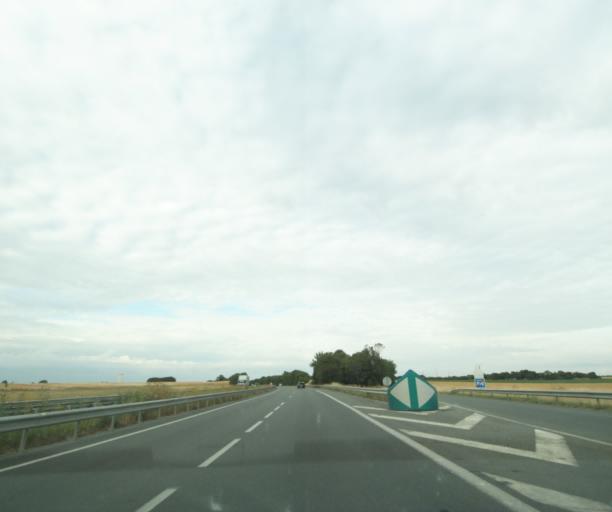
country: FR
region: Poitou-Charentes
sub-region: Departement de la Charente-Maritime
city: Dompierre-sur-Mer
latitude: 46.1837
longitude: -1.0808
